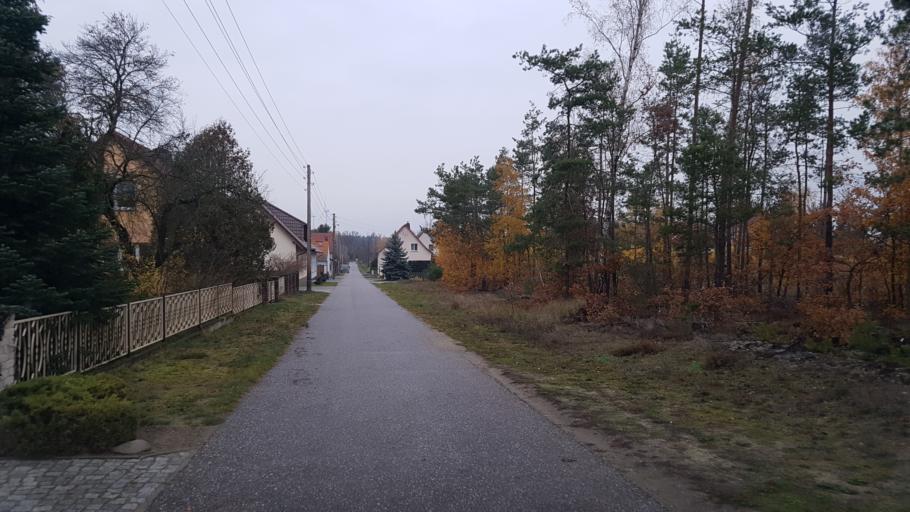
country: DE
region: Brandenburg
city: Schilda
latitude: 51.6419
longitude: 13.3953
